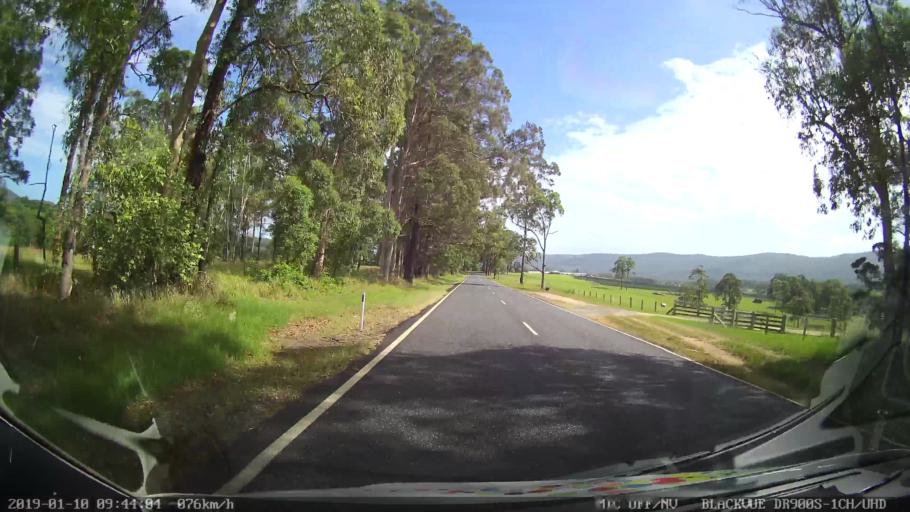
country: AU
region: New South Wales
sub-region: Coffs Harbour
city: Nana Glen
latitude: -30.1211
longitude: 153.0033
